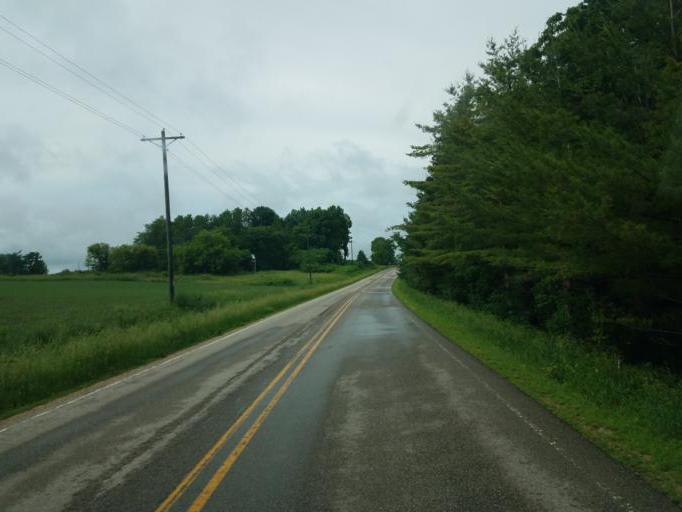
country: US
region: Wisconsin
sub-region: Vernon County
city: Hillsboro
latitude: 43.6797
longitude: -90.4530
